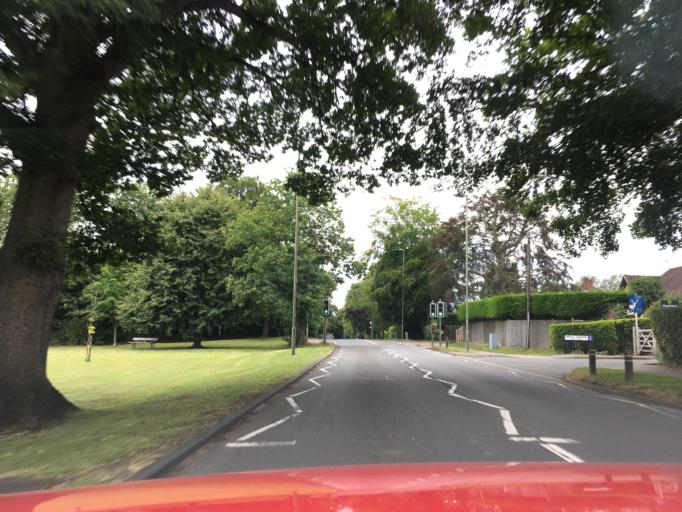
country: GB
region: England
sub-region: Surrey
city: Felbridge
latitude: 51.1401
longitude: -0.0442
